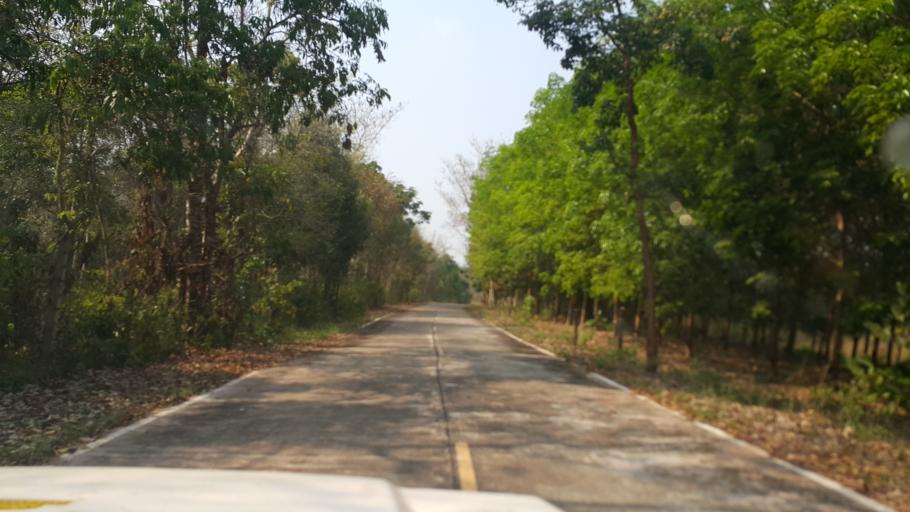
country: TH
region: Nakhon Phanom
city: Ban Phaeng
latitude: 17.9718
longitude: 104.1518
